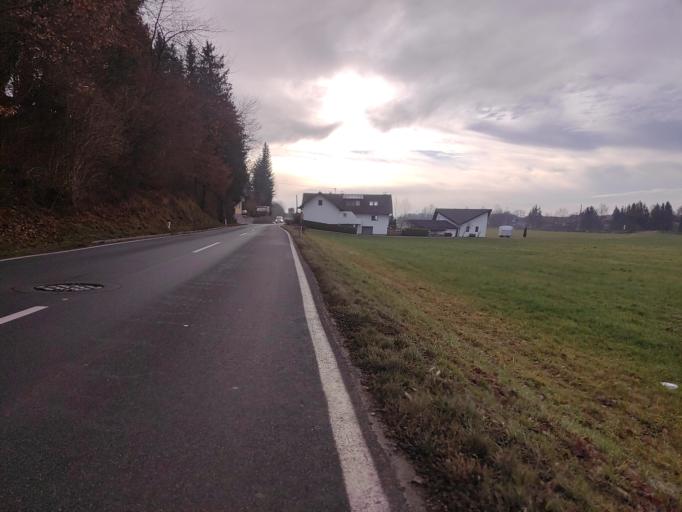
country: AT
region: Salzburg
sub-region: Politischer Bezirk Salzburg-Umgebung
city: Strasswalchen
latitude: 47.9948
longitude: 13.2400
